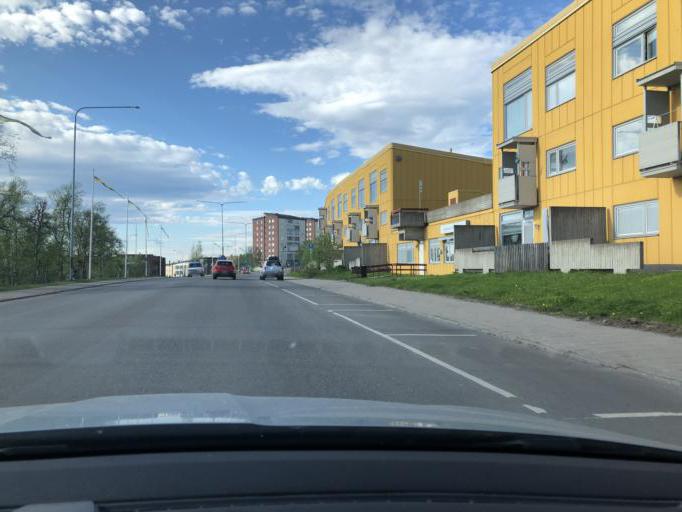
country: SE
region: Norrbotten
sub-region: Kiruna Kommun
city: Kiruna
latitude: 67.8546
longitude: 20.2232
